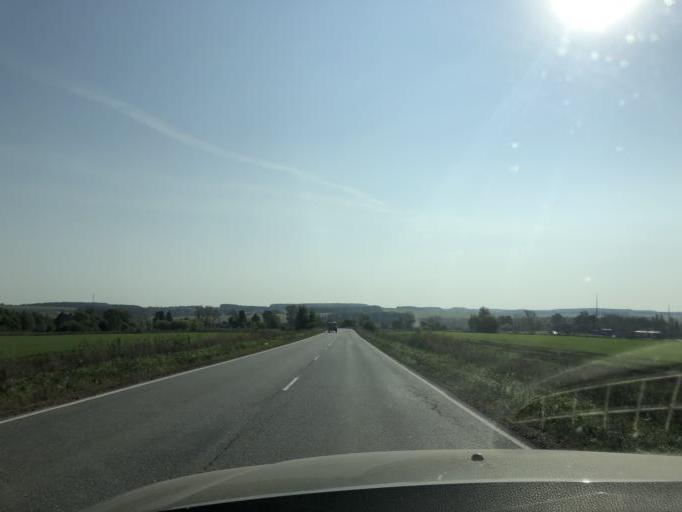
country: RU
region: Tula
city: Novogurovskiy
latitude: 54.4610
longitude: 37.4645
